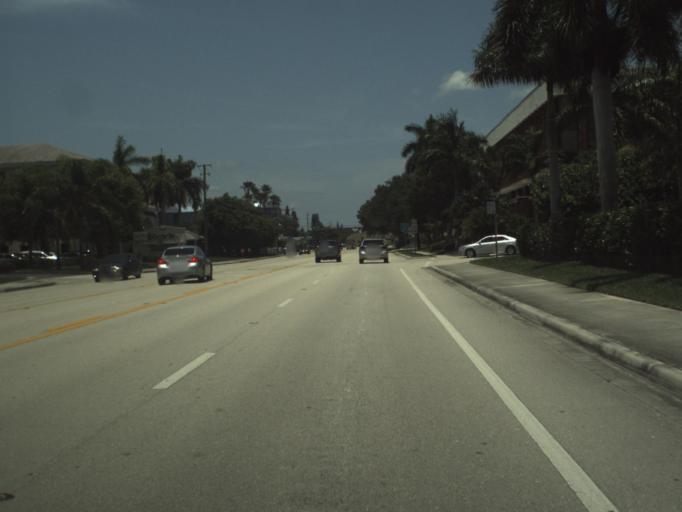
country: US
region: Florida
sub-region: Martin County
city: Sewall's Point
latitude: 27.1945
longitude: -80.2241
